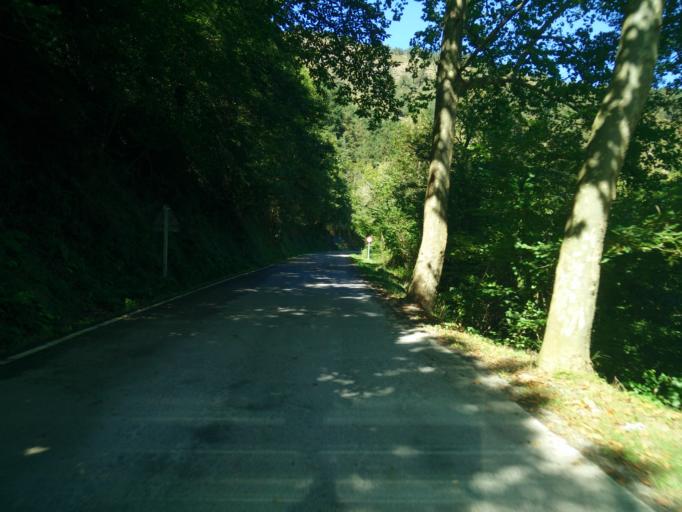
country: ES
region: Cantabria
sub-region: Provincia de Cantabria
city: Ruente
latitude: 43.1458
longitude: -4.2871
